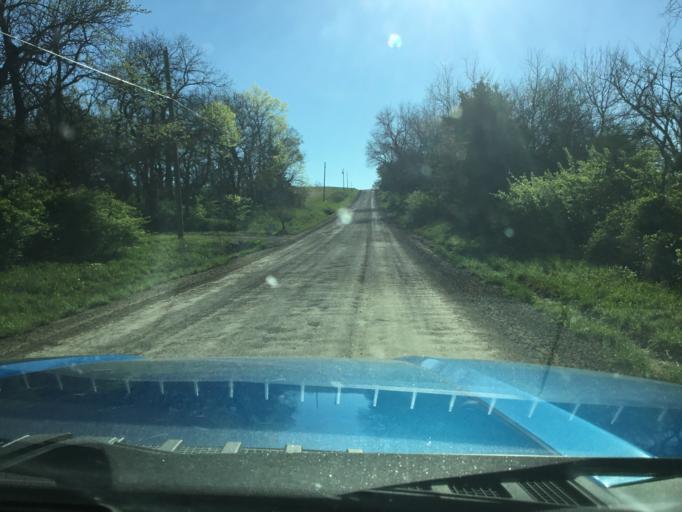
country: US
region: Kansas
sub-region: Douglas County
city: Lawrence
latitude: 38.9569
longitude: -95.3501
